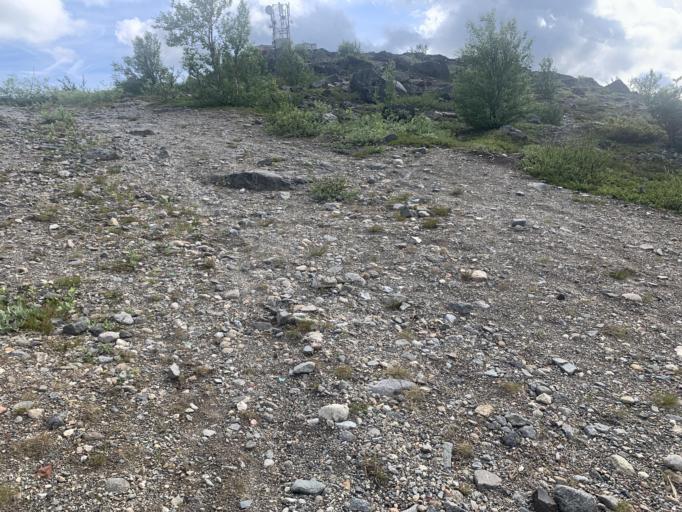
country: RU
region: Murmansk
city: Monchegorsk
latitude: 67.9171
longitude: 32.9779
